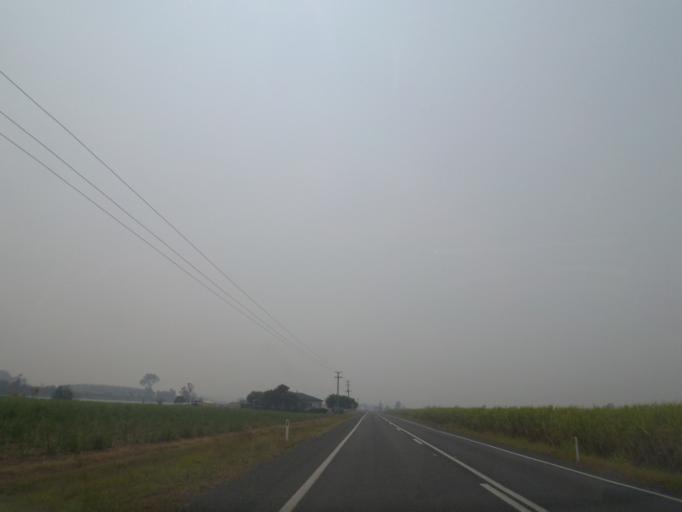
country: AU
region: New South Wales
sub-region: Clarence Valley
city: Maclean
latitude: -29.5649
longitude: 153.1147
